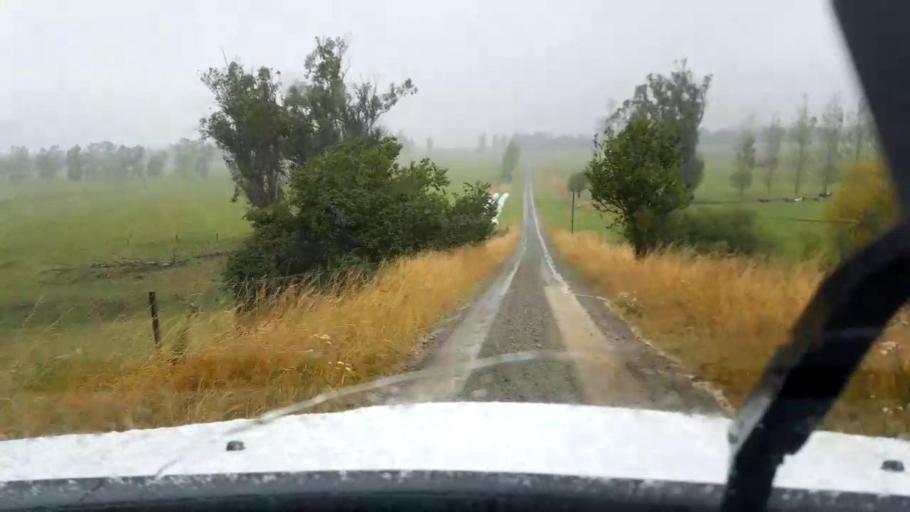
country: NZ
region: Canterbury
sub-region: Timaru District
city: Pleasant Point
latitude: -44.1967
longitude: 171.0912
